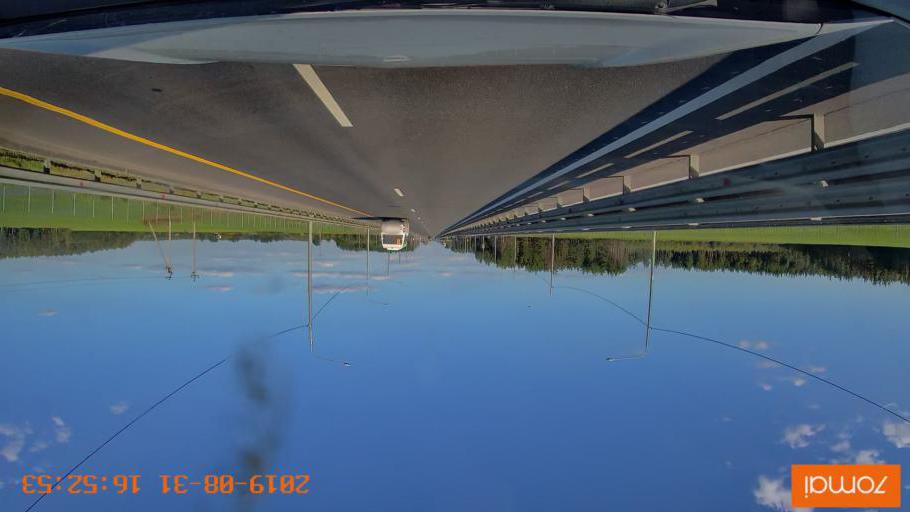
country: RU
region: Kaluga
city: Detchino
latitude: 54.7478
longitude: 36.2006
